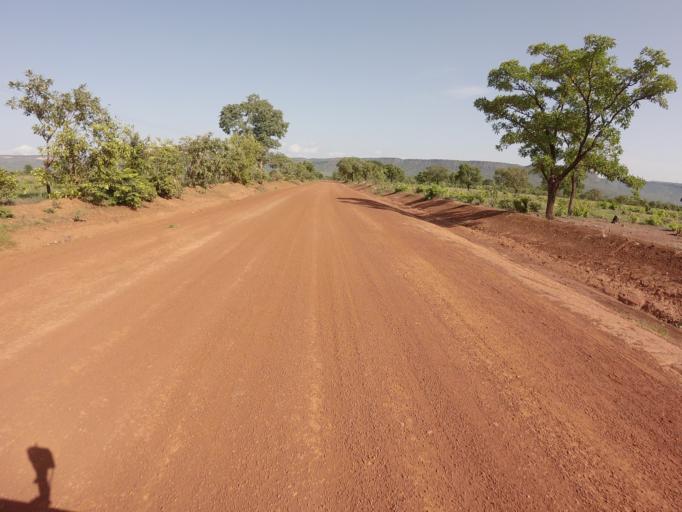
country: GH
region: Upper East
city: Bawku
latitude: 10.6813
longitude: -0.2139
